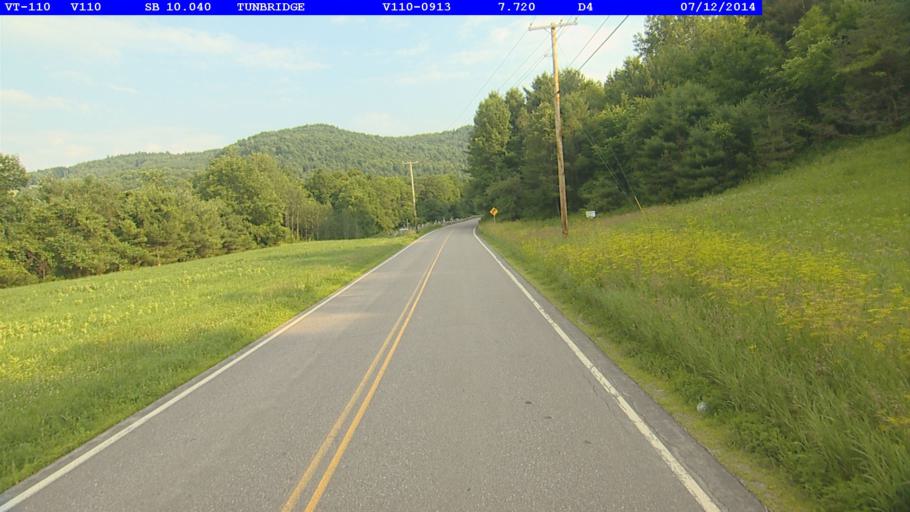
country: US
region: Vermont
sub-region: Orange County
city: Chelsea
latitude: 43.9487
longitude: -72.4603
